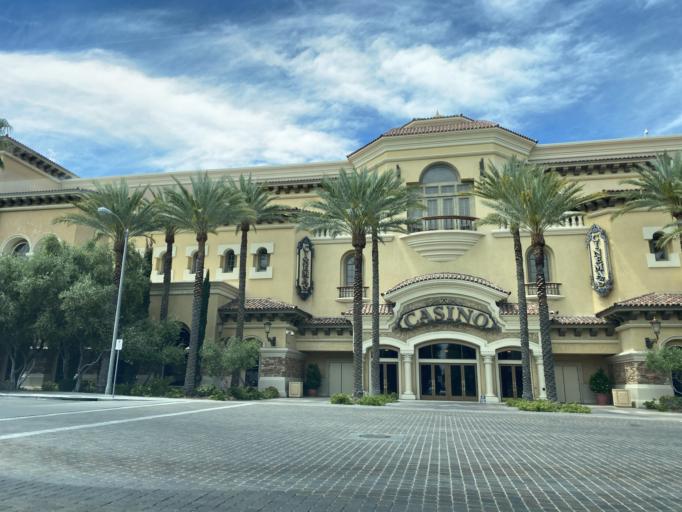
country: US
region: Nevada
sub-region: Clark County
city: Whitney
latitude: 36.0212
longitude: -115.0883
